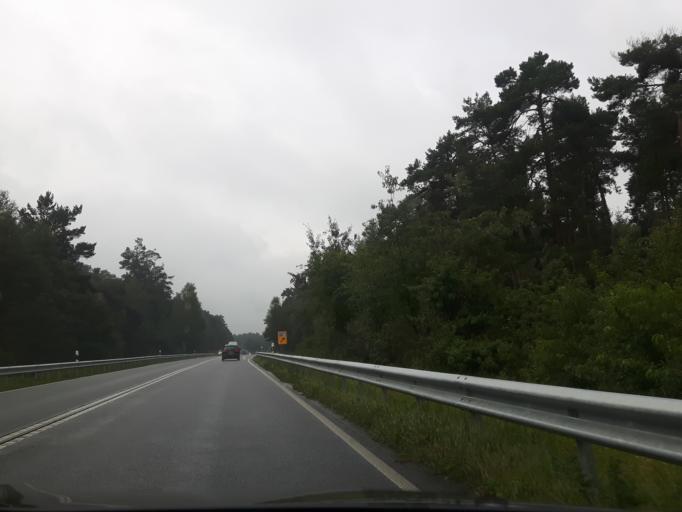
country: DE
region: Lower Saxony
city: Lingen
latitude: 52.5048
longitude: 7.3427
